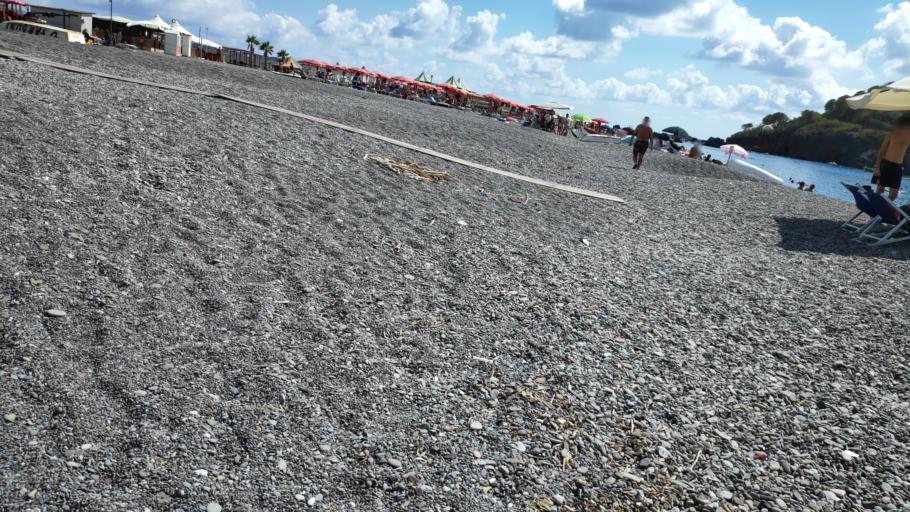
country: IT
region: Calabria
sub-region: Provincia di Cosenza
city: Praia a Mare
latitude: 39.8755
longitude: 15.7834
